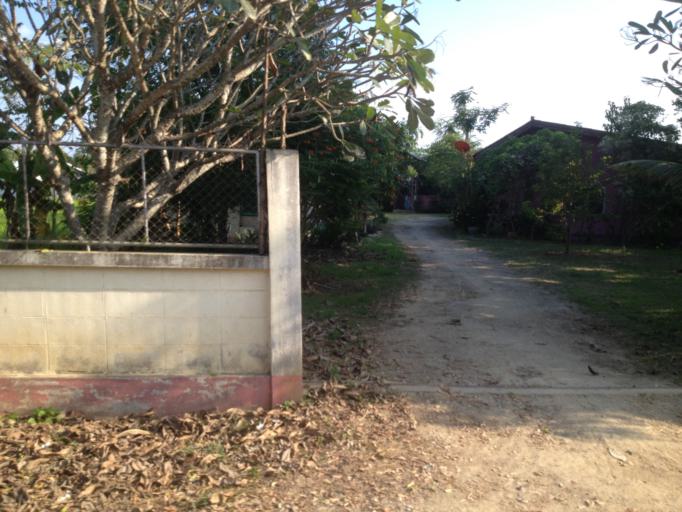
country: TH
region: Chiang Mai
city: Hang Dong
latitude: 18.7156
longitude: 98.9299
